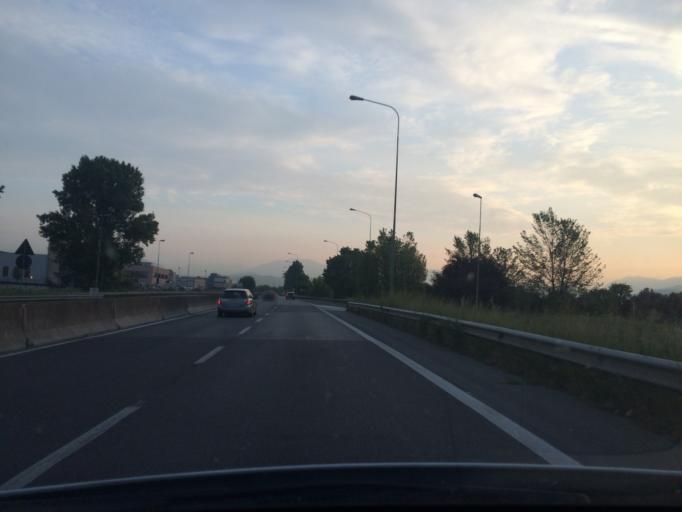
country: IT
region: Lombardy
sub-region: Provincia di Brescia
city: Castel Mella
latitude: 45.5017
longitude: 10.1638
